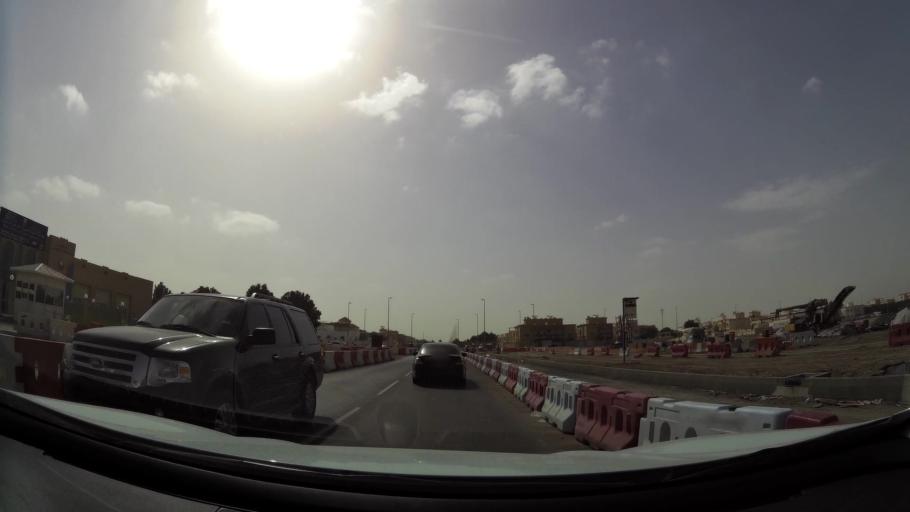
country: AE
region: Abu Dhabi
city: Abu Dhabi
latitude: 24.4241
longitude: 54.5640
